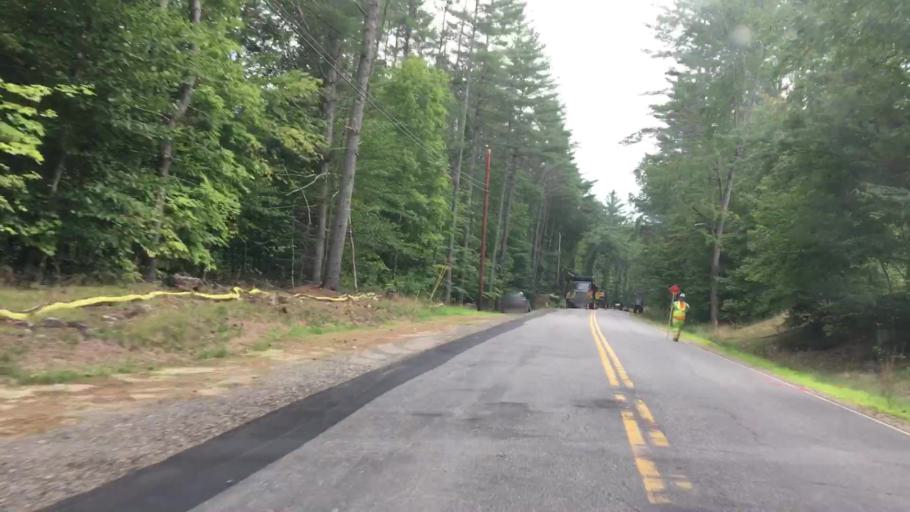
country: US
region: Maine
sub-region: Oxford County
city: Rumford
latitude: 44.5209
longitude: -70.6798
